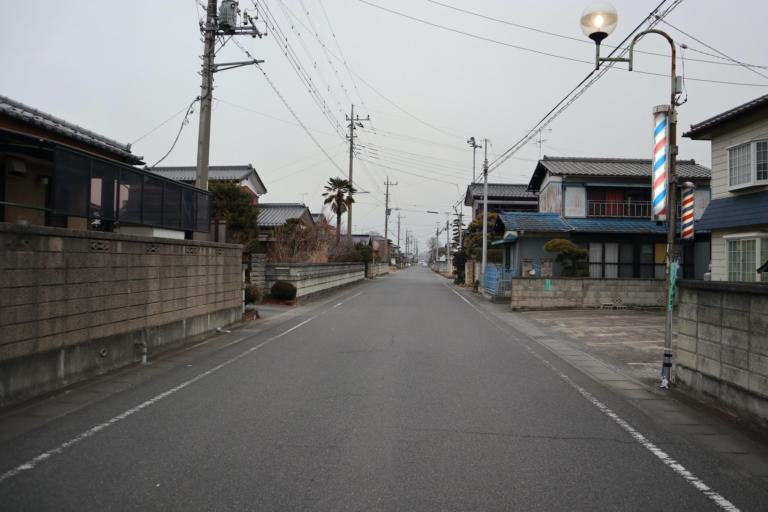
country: JP
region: Saitama
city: Hanyu
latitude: 36.1966
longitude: 139.5142
